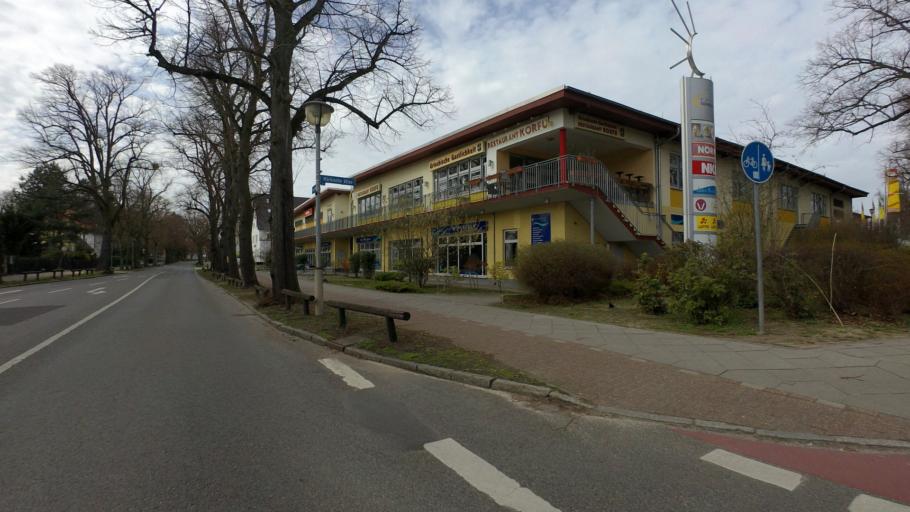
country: DE
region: Brandenburg
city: Glienicke
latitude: 52.6302
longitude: 13.3235
